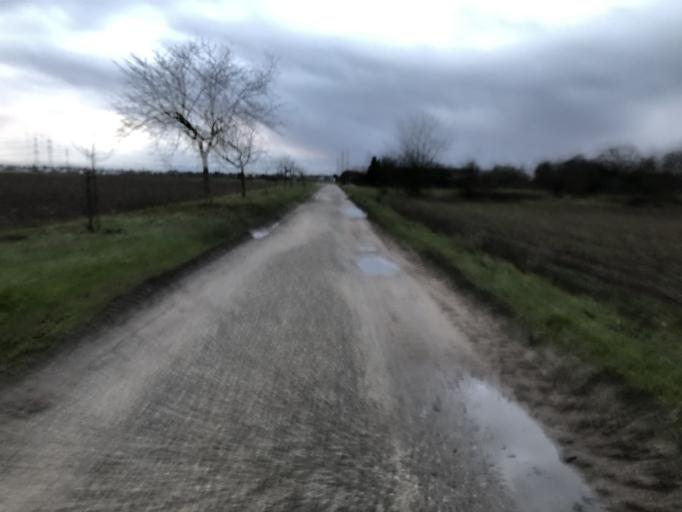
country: DE
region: Baden-Wuerttemberg
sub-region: Karlsruhe Region
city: Neulussheim
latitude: 49.3050
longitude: 8.5227
